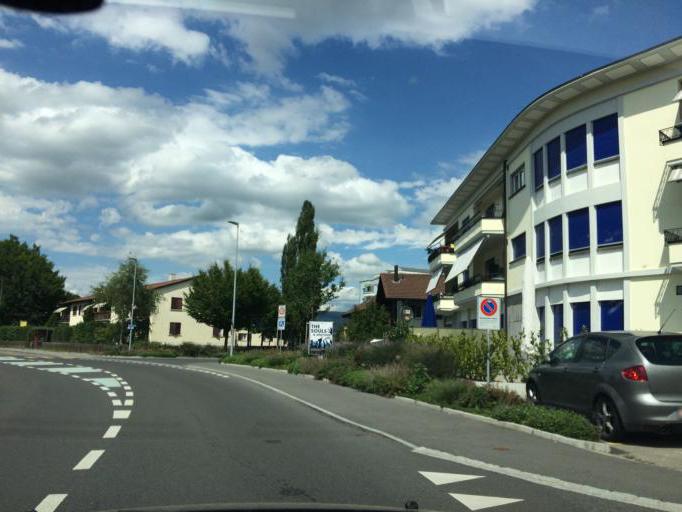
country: CH
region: Bern
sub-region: Thun District
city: Thun
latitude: 46.7409
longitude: 7.6148
